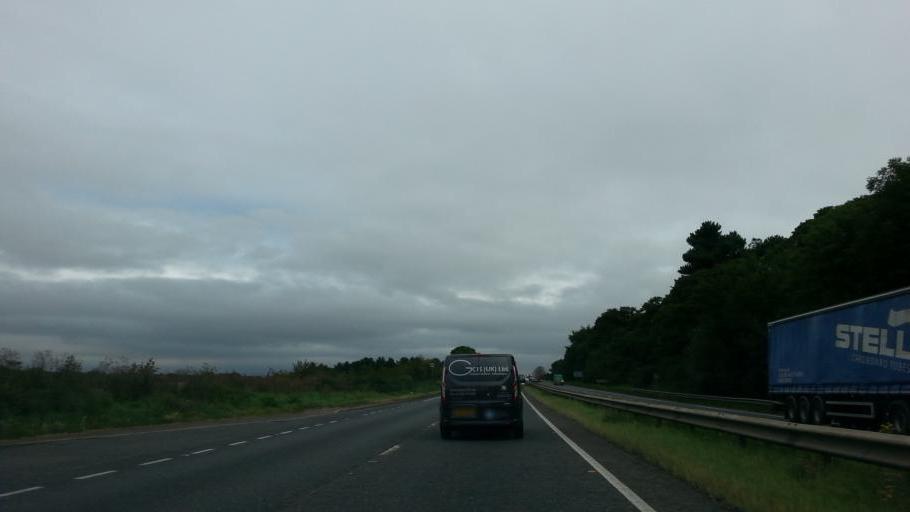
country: GB
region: England
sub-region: Nottinghamshire
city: Babworth
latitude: 53.3117
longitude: -1.0296
